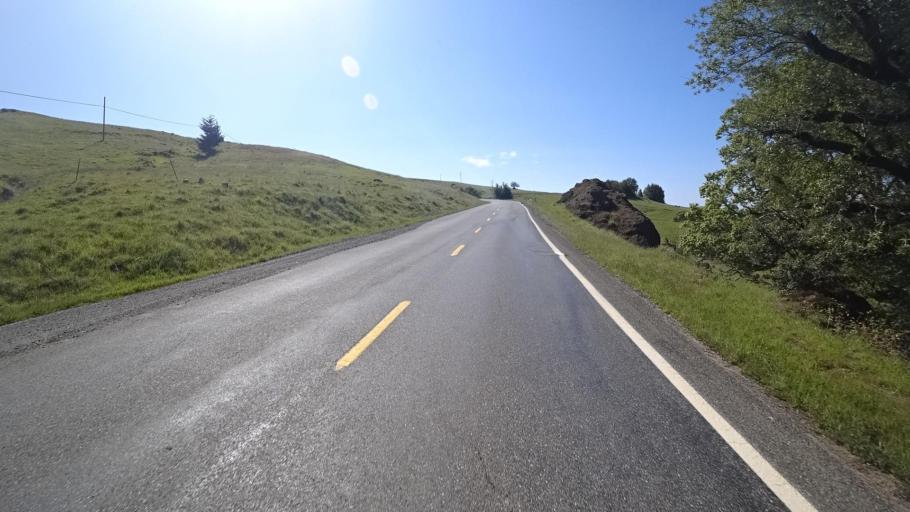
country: US
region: California
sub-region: Humboldt County
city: Redway
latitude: 40.1095
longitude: -123.7166
